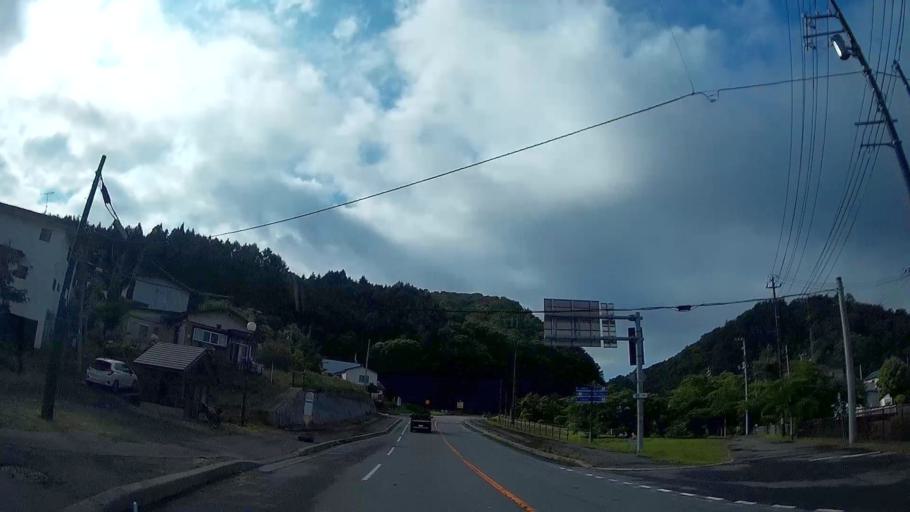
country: JP
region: Hokkaido
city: Date
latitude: 42.5576
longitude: 140.8872
